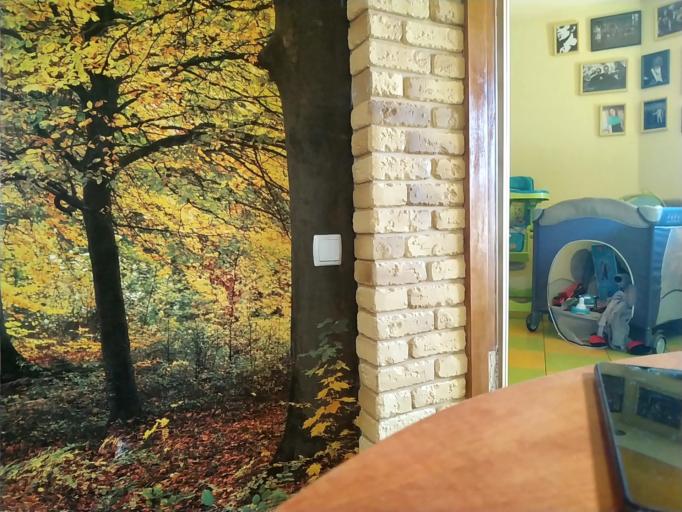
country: RU
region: Tverskaya
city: Velikooktyabr'skiy
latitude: 57.5162
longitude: 34.0611
